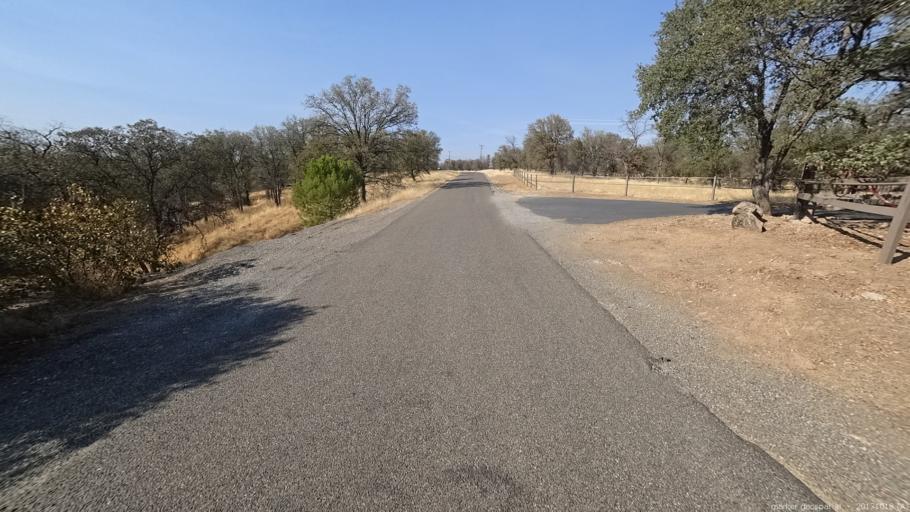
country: US
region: California
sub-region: Shasta County
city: Palo Cedro
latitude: 40.5567
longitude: -122.2539
